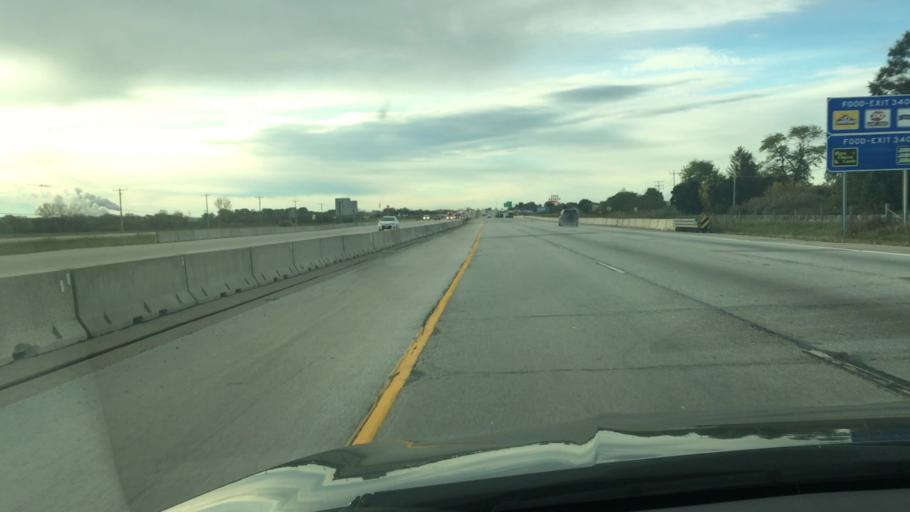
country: US
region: Wisconsin
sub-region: Kenosha County
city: Somers
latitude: 42.6258
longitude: -87.9527
